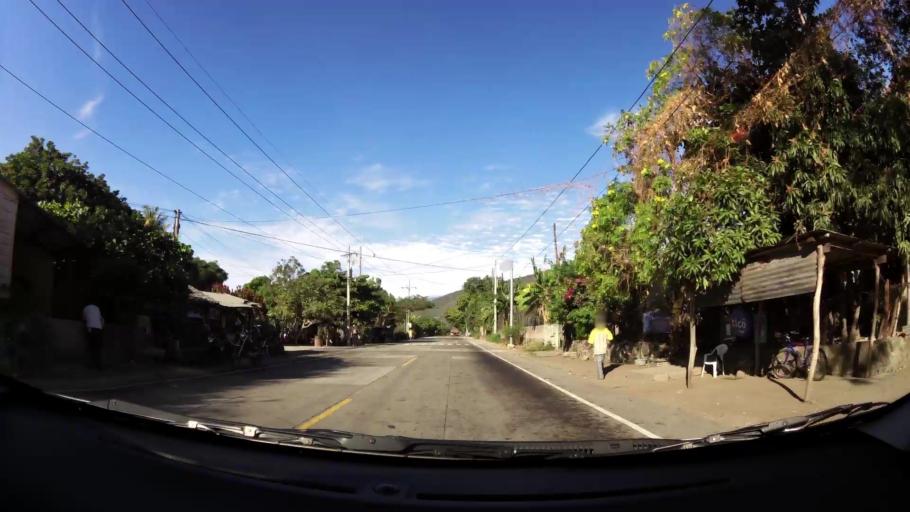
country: SV
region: Santa Ana
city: Metapan
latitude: 14.2437
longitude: -89.4715
